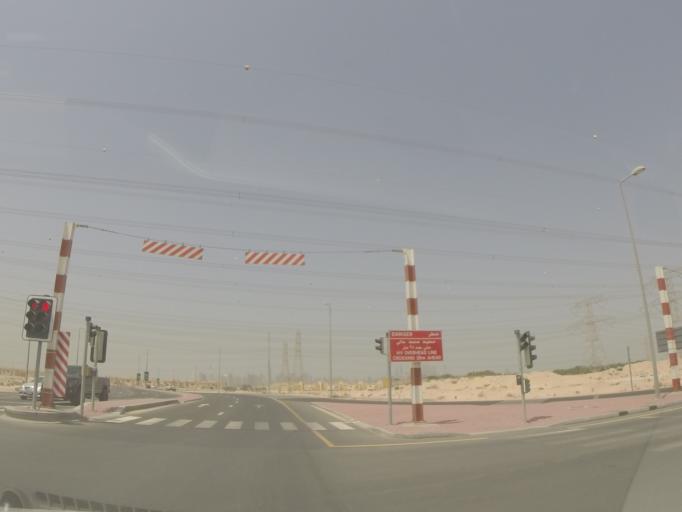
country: AE
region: Dubai
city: Dubai
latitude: 25.0387
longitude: 55.1734
